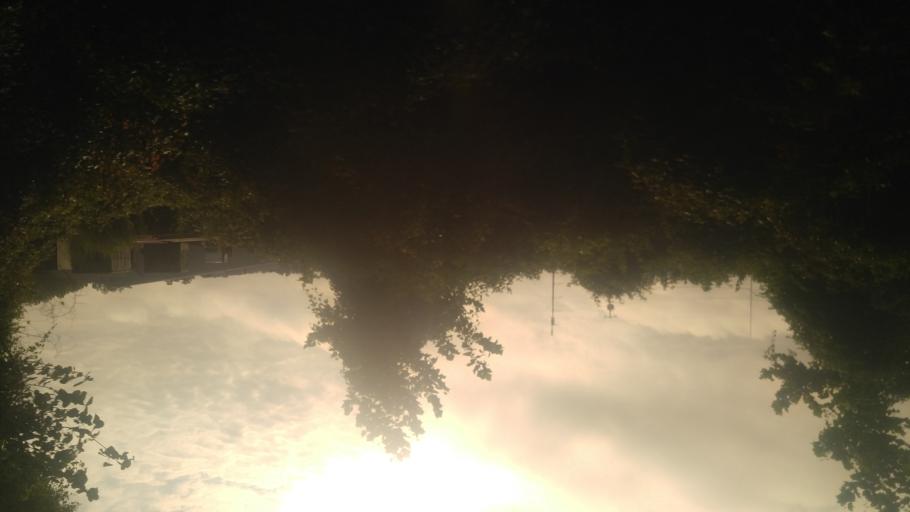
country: US
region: North Carolina
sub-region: Wake County
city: Raleigh
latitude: 35.7549
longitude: -78.6342
